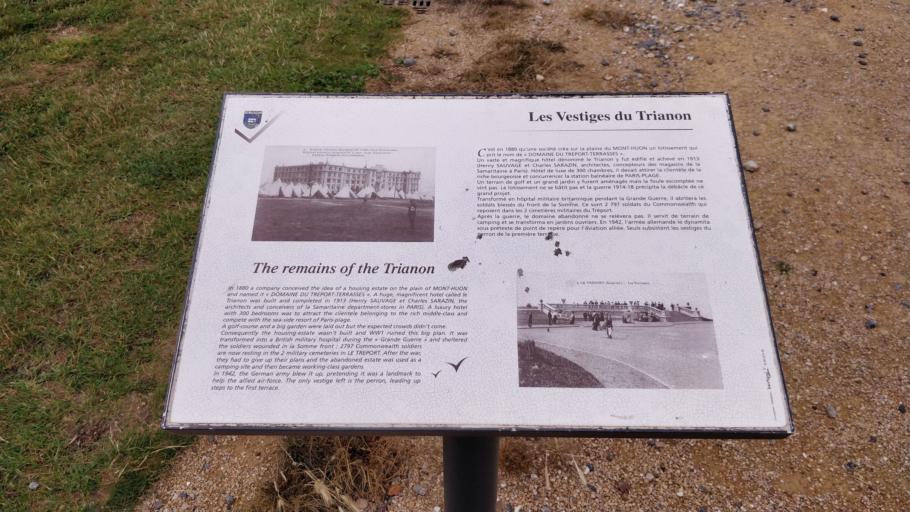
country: FR
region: Haute-Normandie
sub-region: Departement de la Seine-Maritime
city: Le Treport
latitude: 50.0597
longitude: 1.3671
